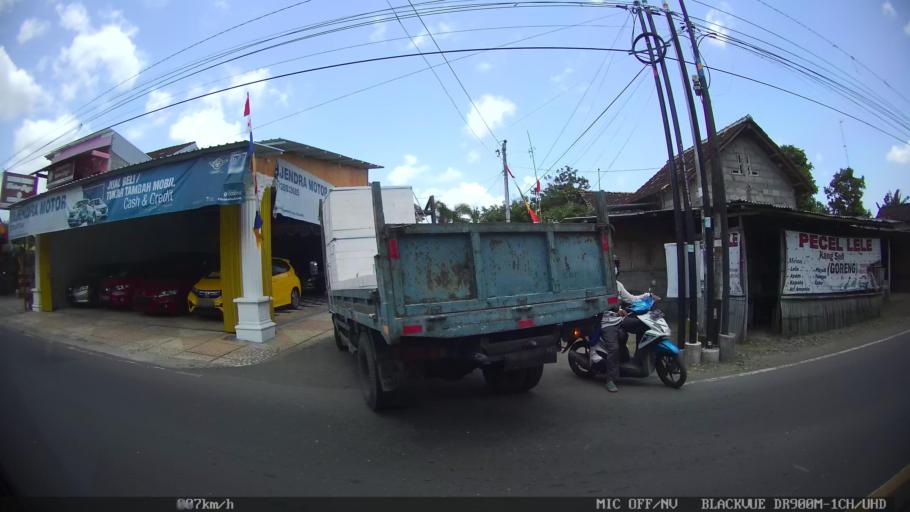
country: ID
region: Daerah Istimewa Yogyakarta
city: Bantul
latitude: -7.9070
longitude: 110.3419
